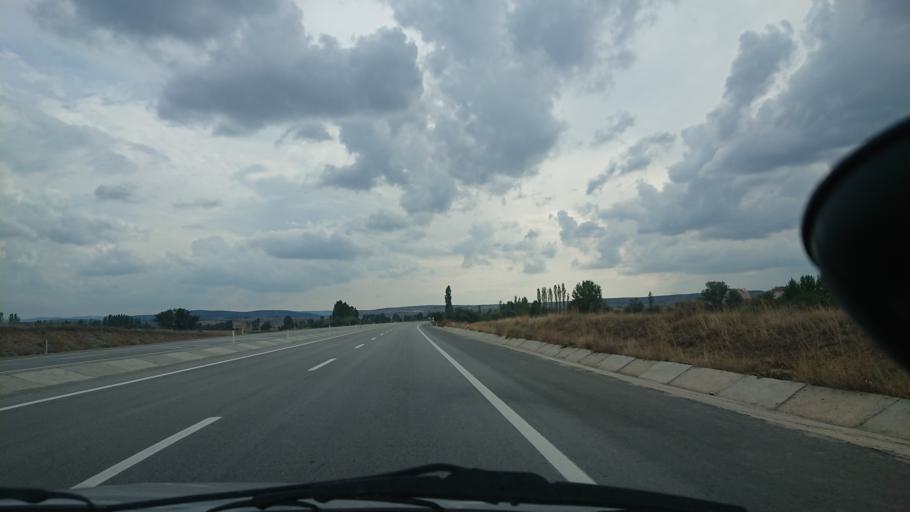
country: TR
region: Kuetahya
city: Cavdarhisar
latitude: 39.1872
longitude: 29.6196
